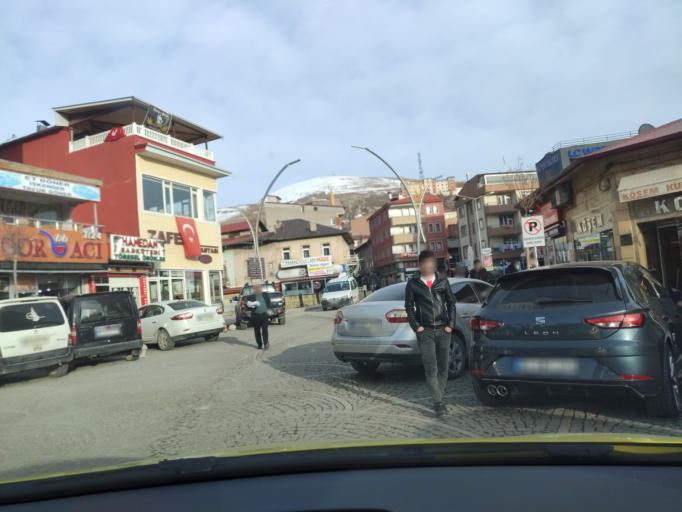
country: TR
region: Bayburt
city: Bayburt
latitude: 40.2604
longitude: 40.2273
